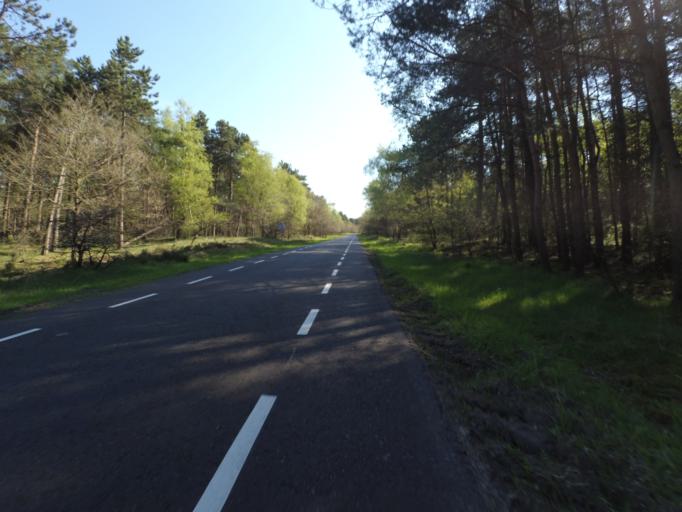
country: NL
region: Gelderland
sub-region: Gemeente Barneveld
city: Stroe
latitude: 52.1681
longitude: 5.7291
